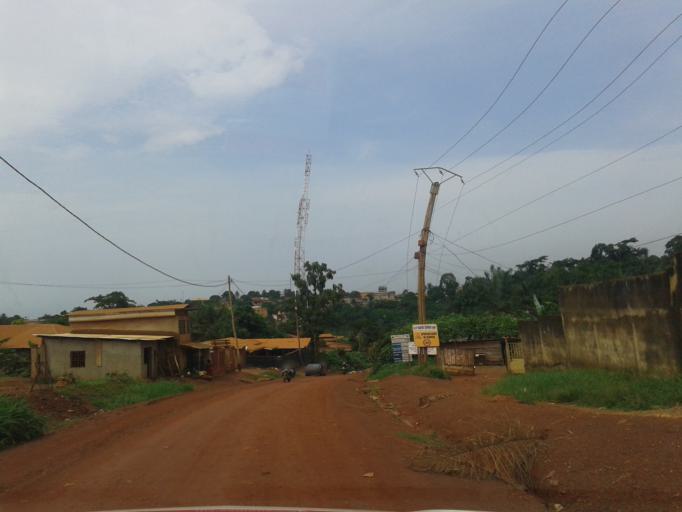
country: CM
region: Centre
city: Yaounde
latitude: 3.9236
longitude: 11.5103
